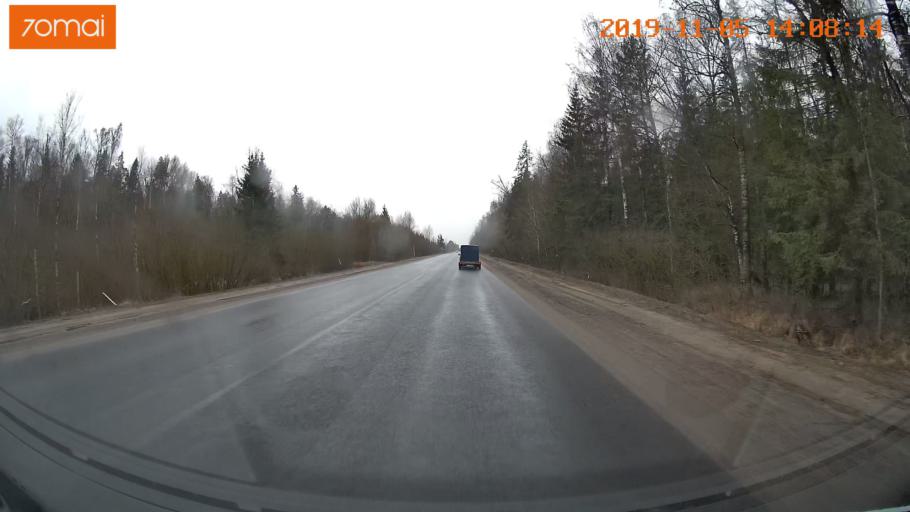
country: RU
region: Ivanovo
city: Kokhma
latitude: 56.9880
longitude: 41.1080
